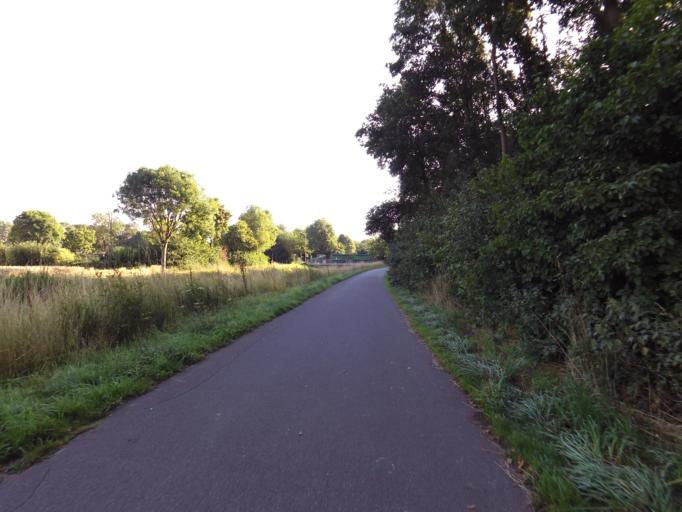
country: DE
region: North Rhine-Westphalia
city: Geilenkirchen
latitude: 50.9794
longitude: 6.1453
